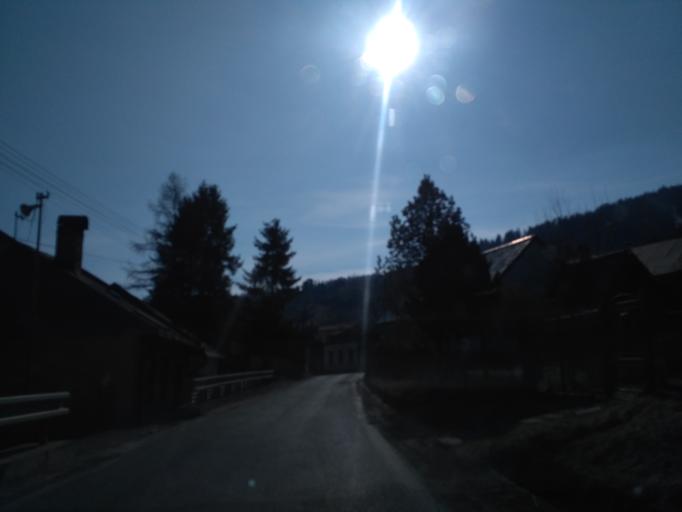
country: SK
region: Kosicky
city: Medzev
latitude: 48.7280
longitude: 20.7341
